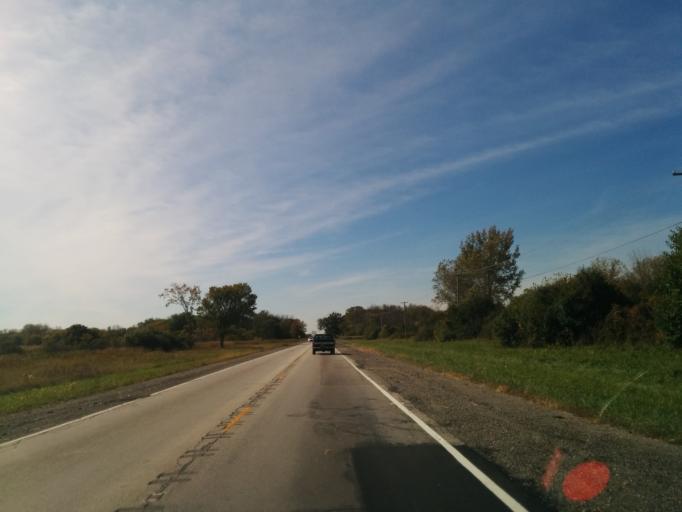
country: US
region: Illinois
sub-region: DuPage County
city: Warrenville
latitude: 41.8193
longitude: -88.2357
